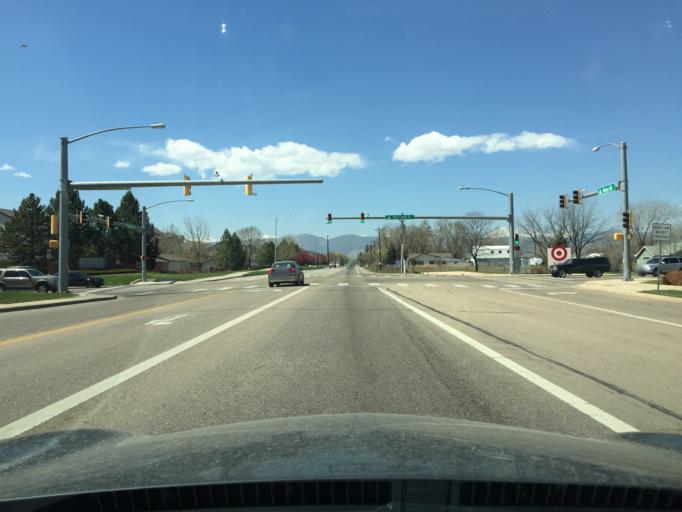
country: US
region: Colorado
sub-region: Boulder County
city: Longmont
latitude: 40.1525
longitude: -105.1344
